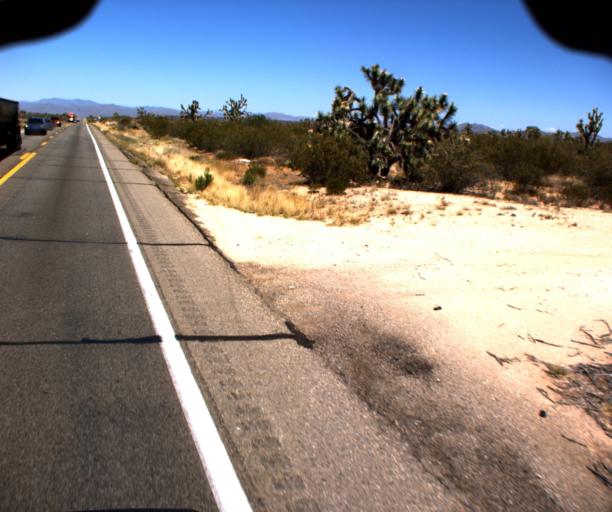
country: US
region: Arizona
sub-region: Yavapai County
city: Congress
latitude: 34.2459
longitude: -113.0793
